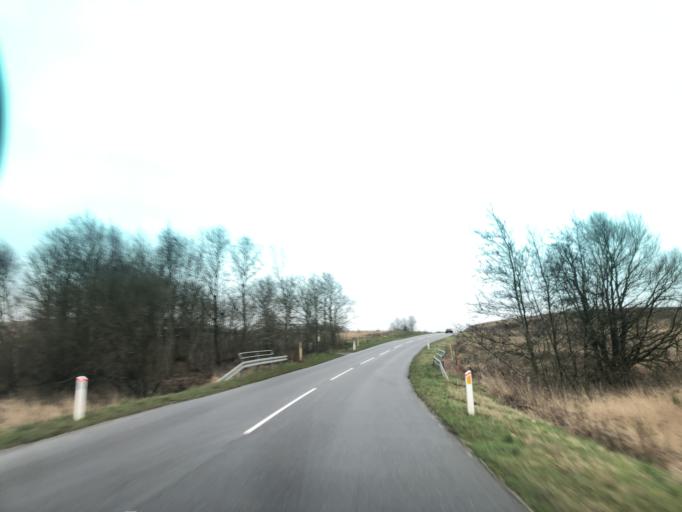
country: DK
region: Central Jutland
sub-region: Randers Kommune
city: Randers
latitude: 56.4216
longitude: 10.0692
